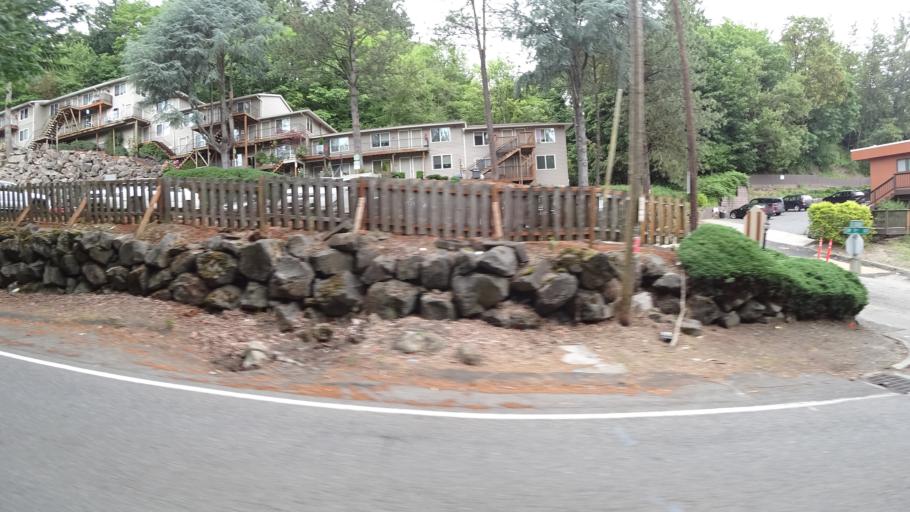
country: US
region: Oregon
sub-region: Multnomah County
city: Portland
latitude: 45.5036
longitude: -122.6890
